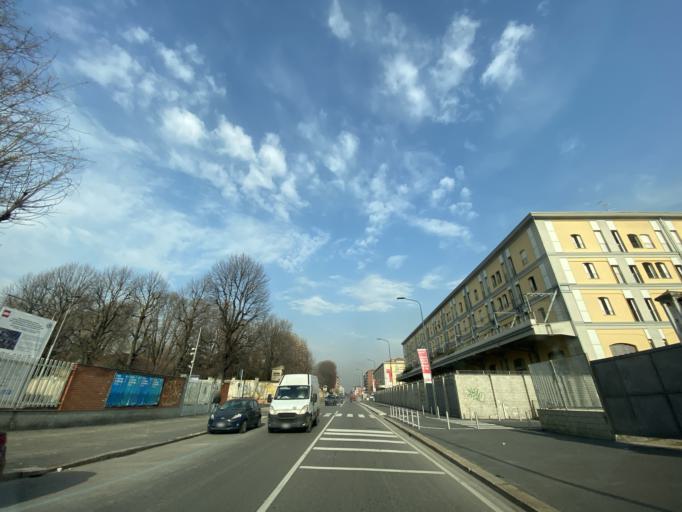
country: IT
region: Lombardy
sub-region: Citta metropolitana di Milano
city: Bresso
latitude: 45.5128
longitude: 9.2014
